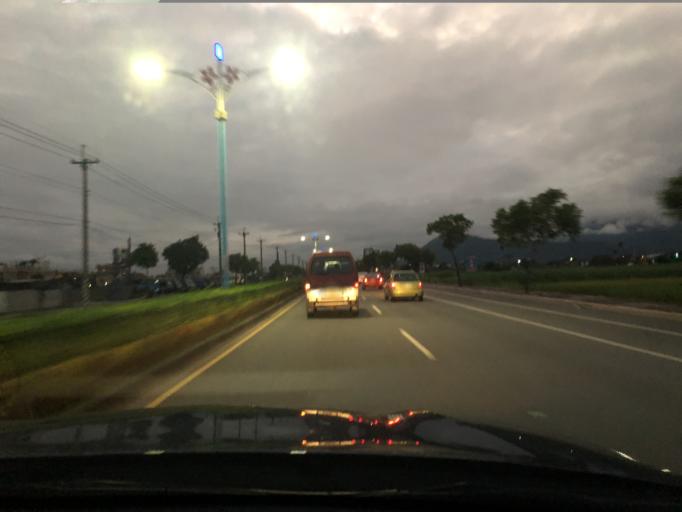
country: TW
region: Taiwan
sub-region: Hualien
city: Hualian
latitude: 23.9683
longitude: 121.5694
